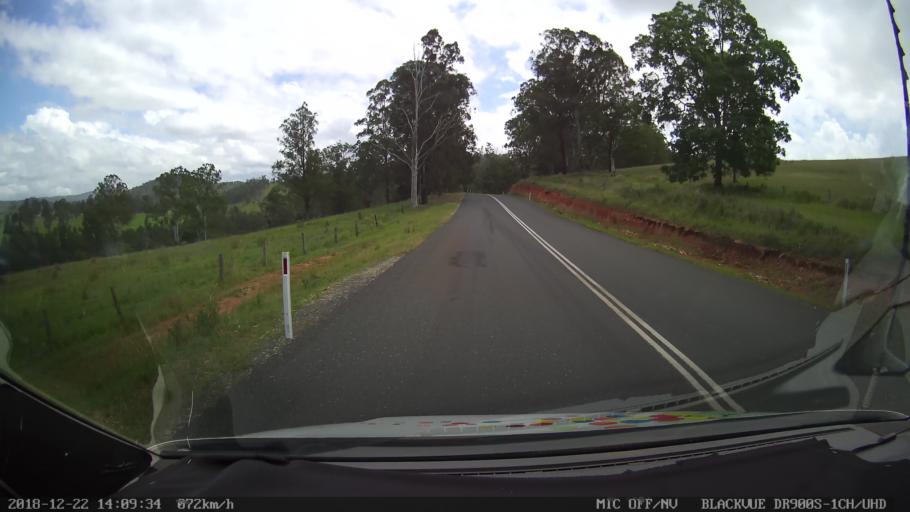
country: AU
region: New South Wales
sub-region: Clarence Valley
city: Coutts Crossing
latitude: -29.9876
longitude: 152.7160
